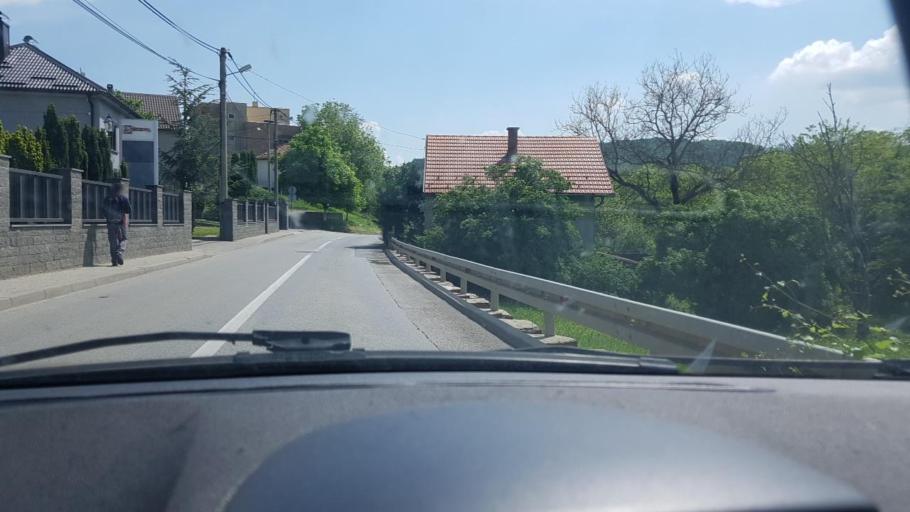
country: HR
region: Grad Zagreb
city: Kasina
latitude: 45.8734
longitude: 16.0159
